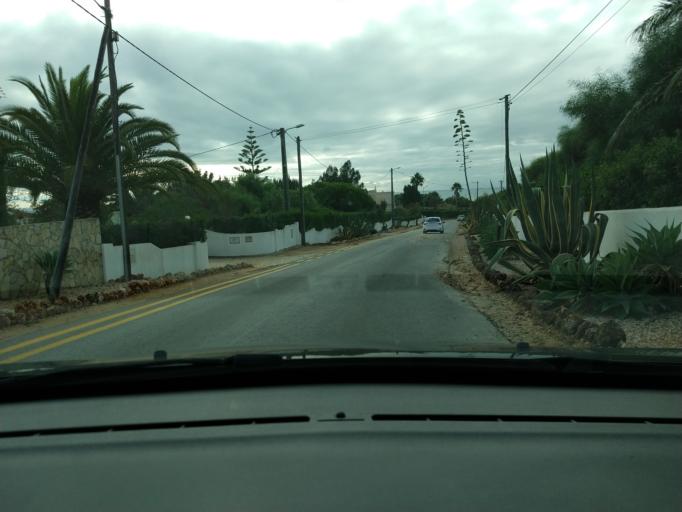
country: PT
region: Faro
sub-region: Lagoa
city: Carvoeiro
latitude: 37.0938
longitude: -8.4152
